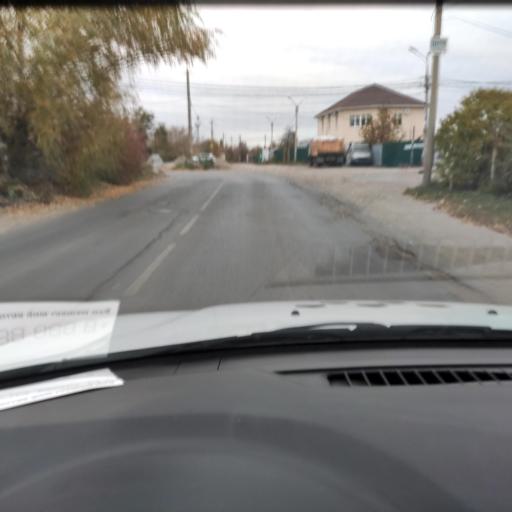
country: RU
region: Samara
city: Tol'yatti
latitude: 53.5368
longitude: 49.4281
